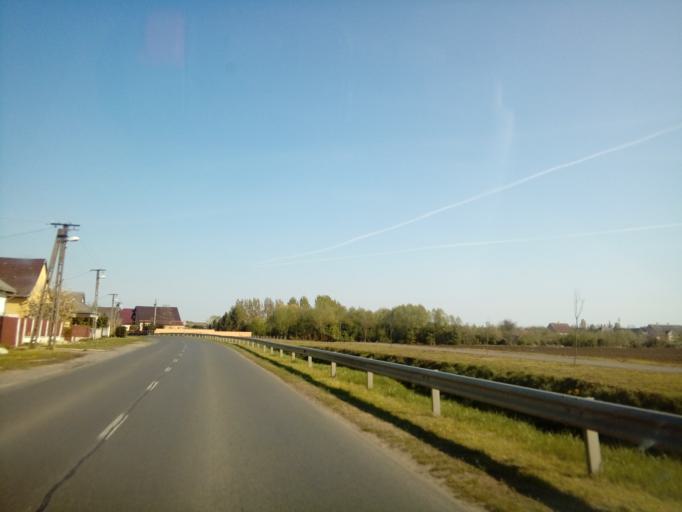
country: HU
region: Szabolcs-Szatmar-Bereg
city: Balkany
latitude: 47.8151
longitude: 21.8510
